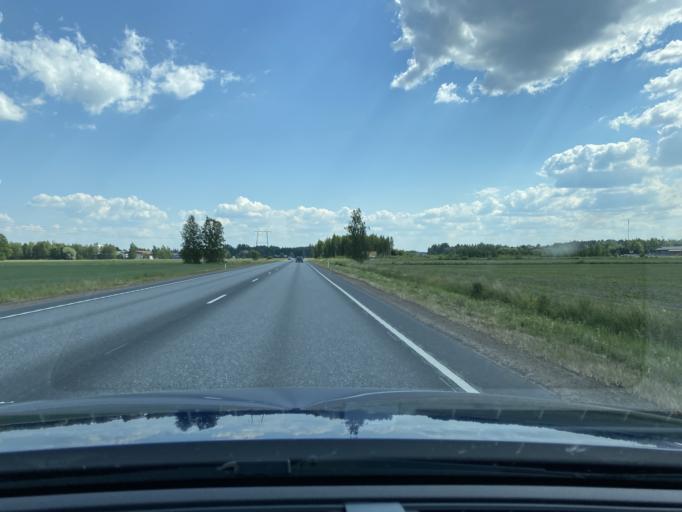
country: FI
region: Satakunta
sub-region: Rauma
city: Eura
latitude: 61.1431
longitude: 22.1096
